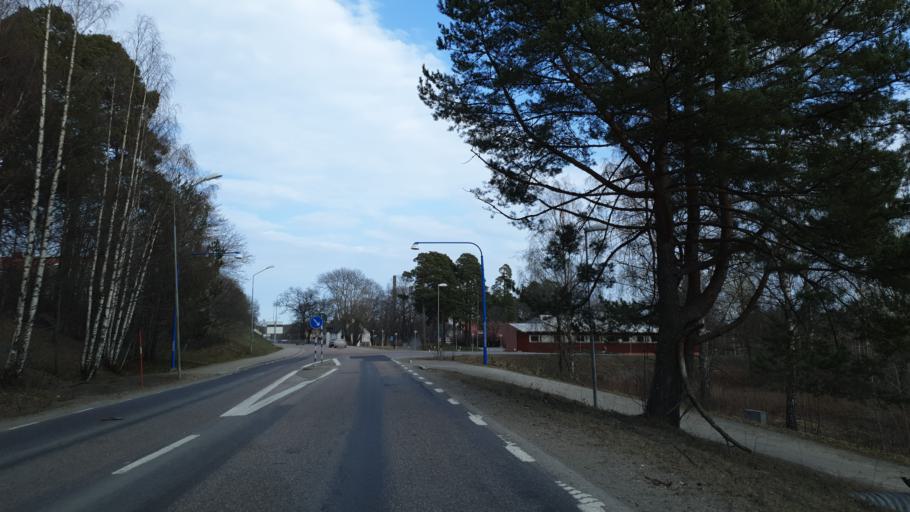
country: SE
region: Gaevleborg
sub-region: Hudiksvalls Kommun
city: Iggesund
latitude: 61.6409
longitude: 17.0723
